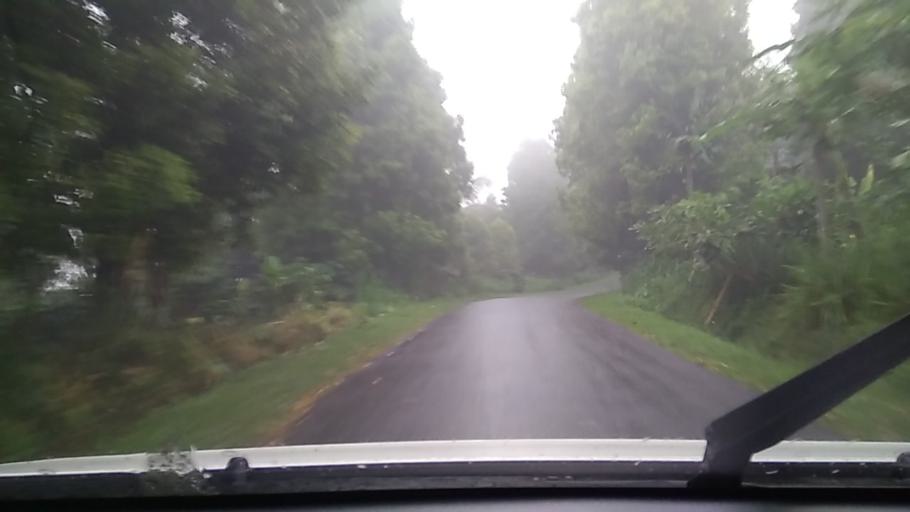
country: ID
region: Bali
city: Banjar Ambengan
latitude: -8.1971
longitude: 115.1783
